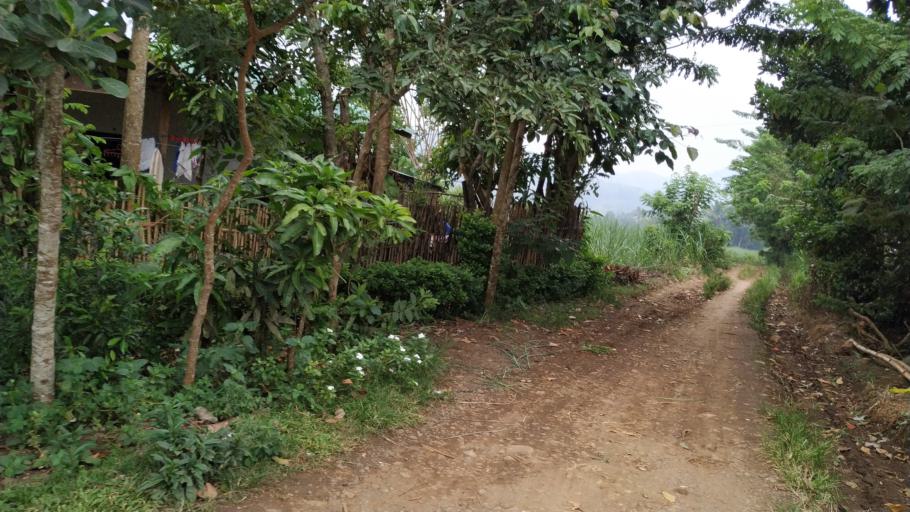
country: PH
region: Western Visayas
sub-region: Province of Negros Occidental
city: Quezon
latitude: 10.4238
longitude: 123.2382
